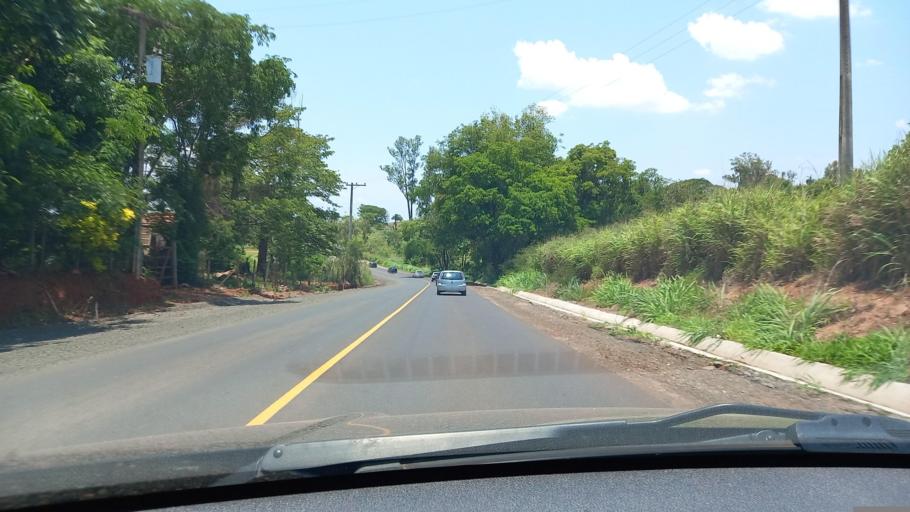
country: BR
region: Sao Paulo
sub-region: Moji-Guacu
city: Mogi-Gaucu
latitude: -22.3473
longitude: -46.8778
